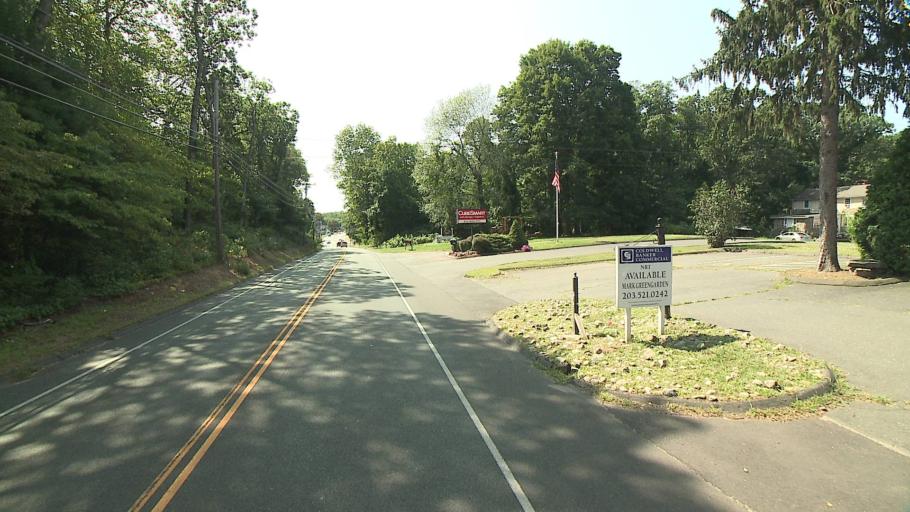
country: US
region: Connecticut
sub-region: Fairfield County
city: Newtown
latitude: 41.3511
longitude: -73.2605
